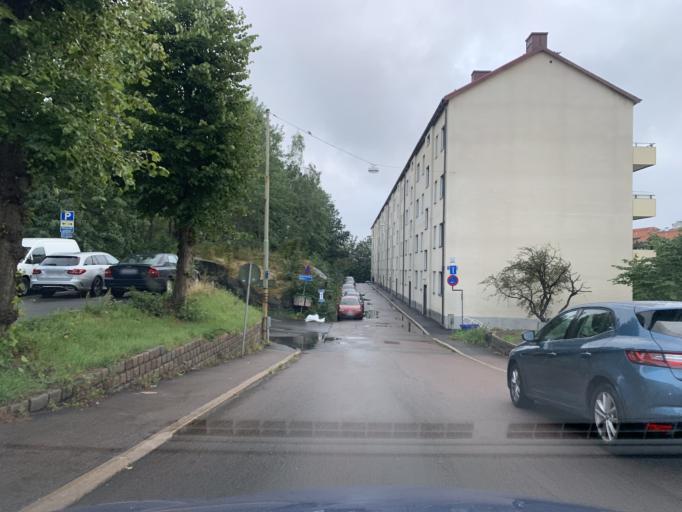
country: SE
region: Vaestra Goetaland
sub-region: Goteborg
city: Goeteborg
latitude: 57.7119
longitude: 12.0122
